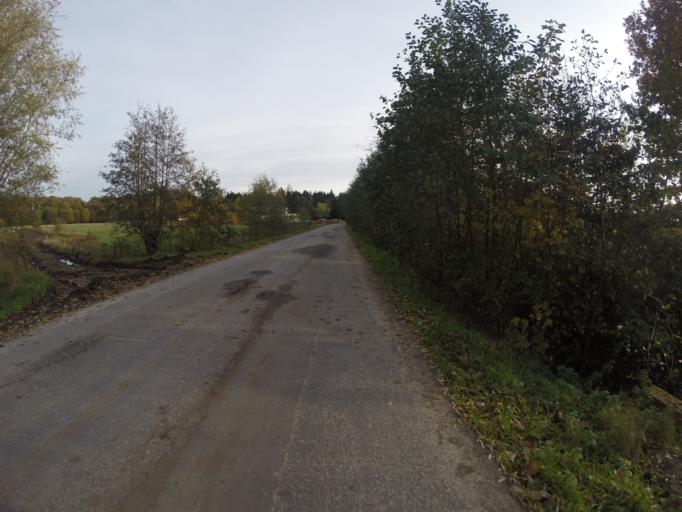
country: BE
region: Flanders
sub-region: Provincie Oost-Vlaanderen
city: Aalter
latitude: 51.0759
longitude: 3.4524
